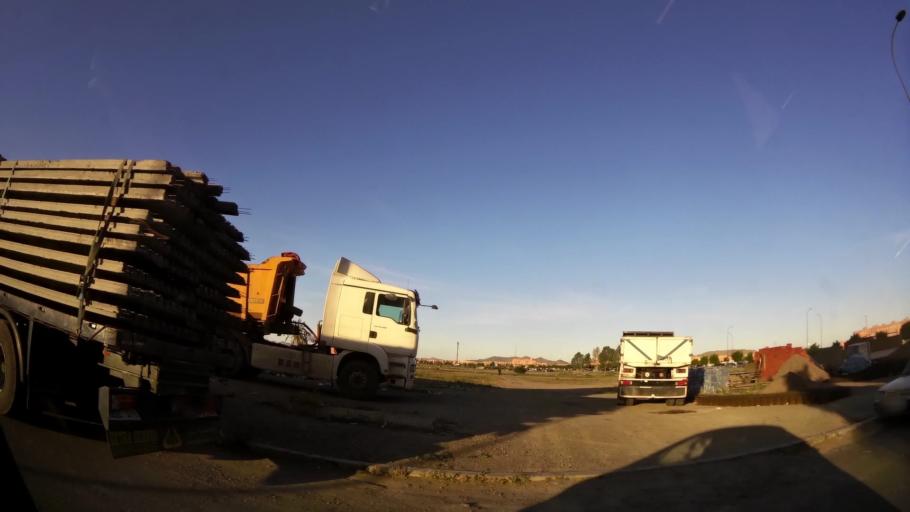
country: MA
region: Marrakech-Tensift-Al Haouz
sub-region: Marrakech
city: Marrakesh
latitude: 31.7527
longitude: -8.1160
